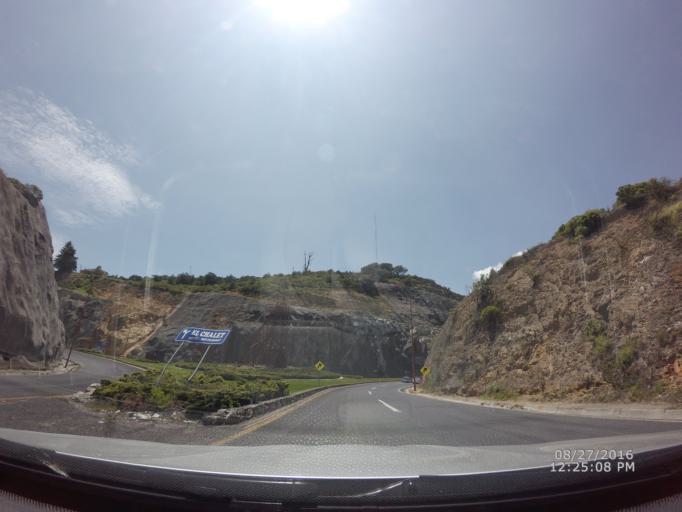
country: MX
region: Hidalgo
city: Mineral del Monte
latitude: 20.1388
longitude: -98.6907
